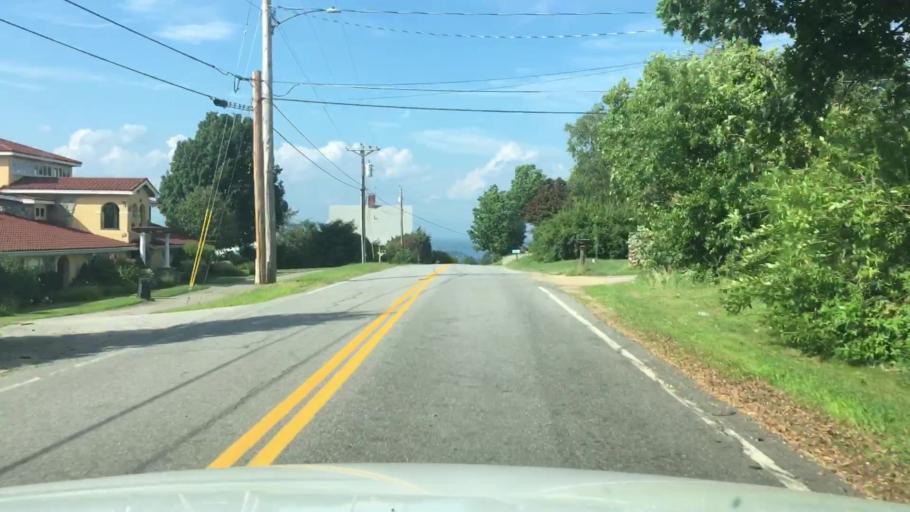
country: US
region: New Hampshire
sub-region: Belknap County
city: Gilford
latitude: 43.5557
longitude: -71.4157
